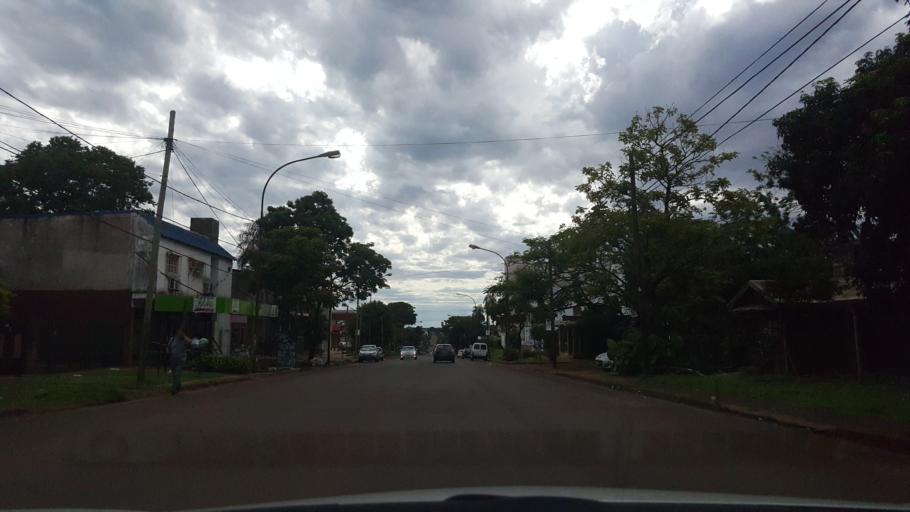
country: AR
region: Misiones
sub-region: Departamento de Capital
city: Posadas
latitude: -27.3712
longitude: -55.9267
